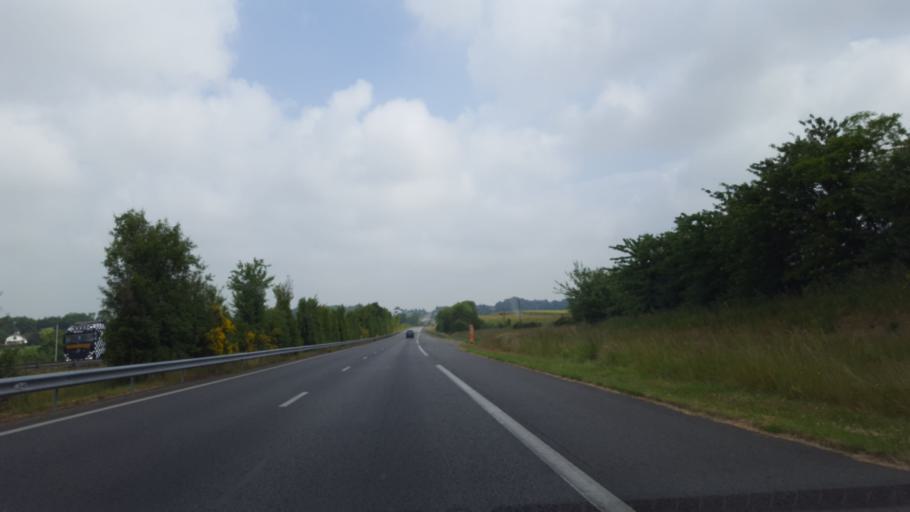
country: FR
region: Brittany
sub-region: Departement d'Ille-et-Vilaine
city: Crevin
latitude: 47.9151
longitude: -1.6813
